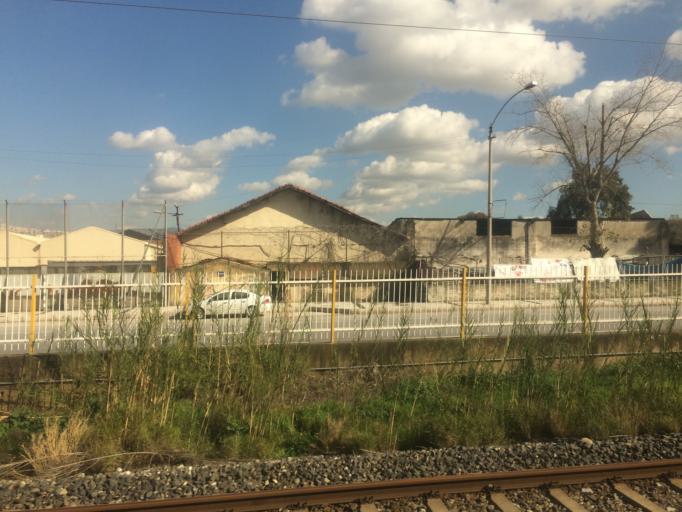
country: TR
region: Izmir
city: Izmir
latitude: 38.4561
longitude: 27.1695
